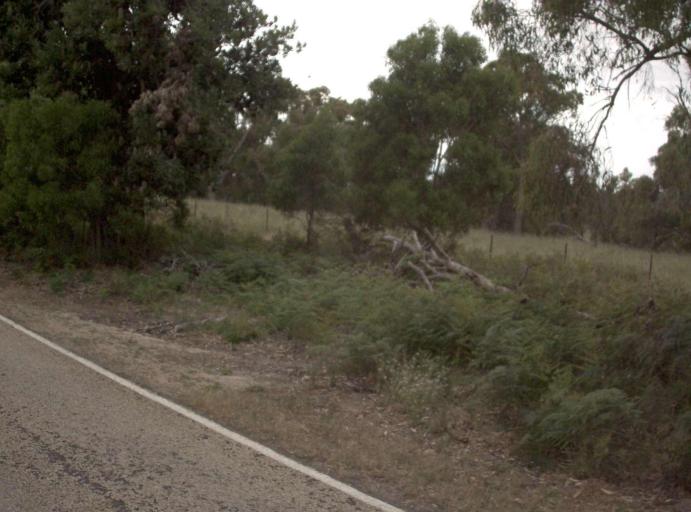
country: AU
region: Victoria
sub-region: Wellington
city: Sale
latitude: -38.0055
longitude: 147.2836
